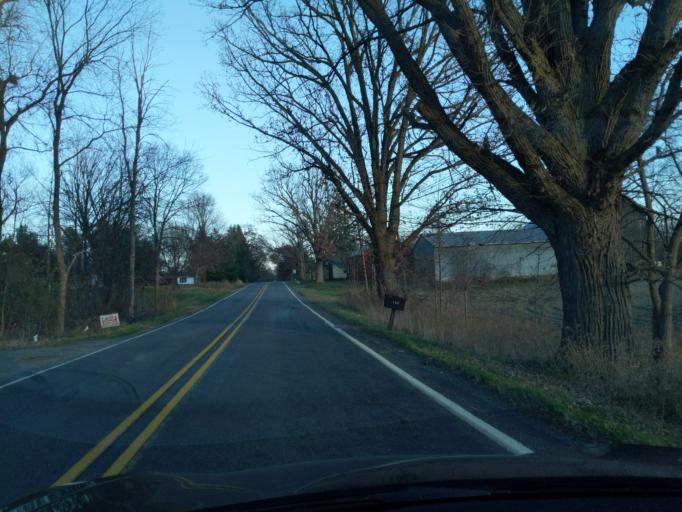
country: US
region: Michigan
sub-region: Ingham County
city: Williamston
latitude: 42.7155
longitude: -84.3372
